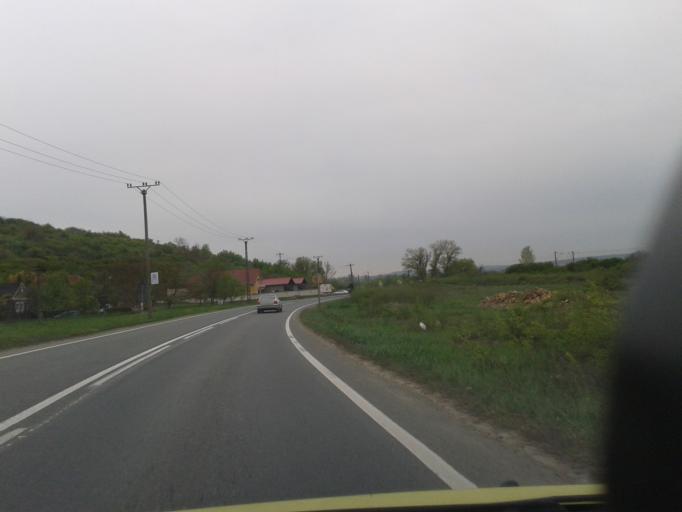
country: RO
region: Arad
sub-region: Comuna Zabrani
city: Neudorf
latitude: 46.1060
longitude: 21.6385
